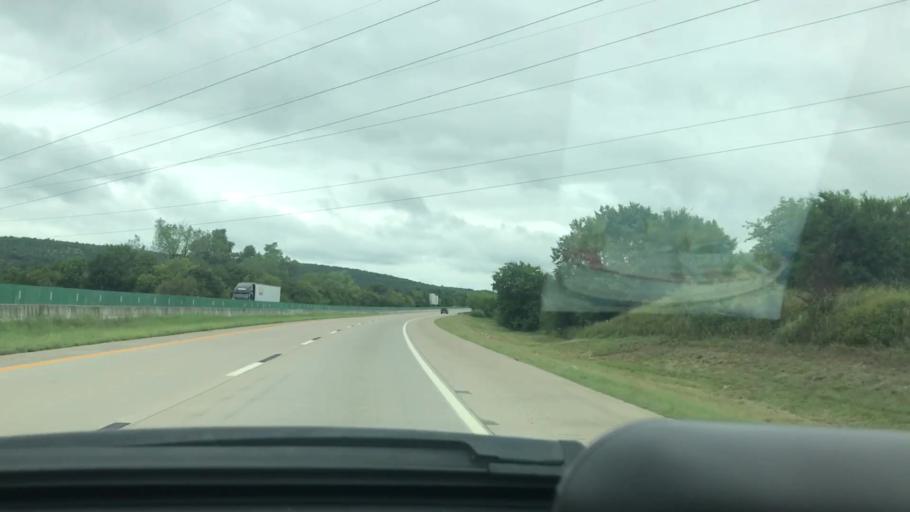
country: US
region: Oklahoma
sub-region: Pittsburg County
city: Krebs
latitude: 35.0133
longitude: -95.7187
